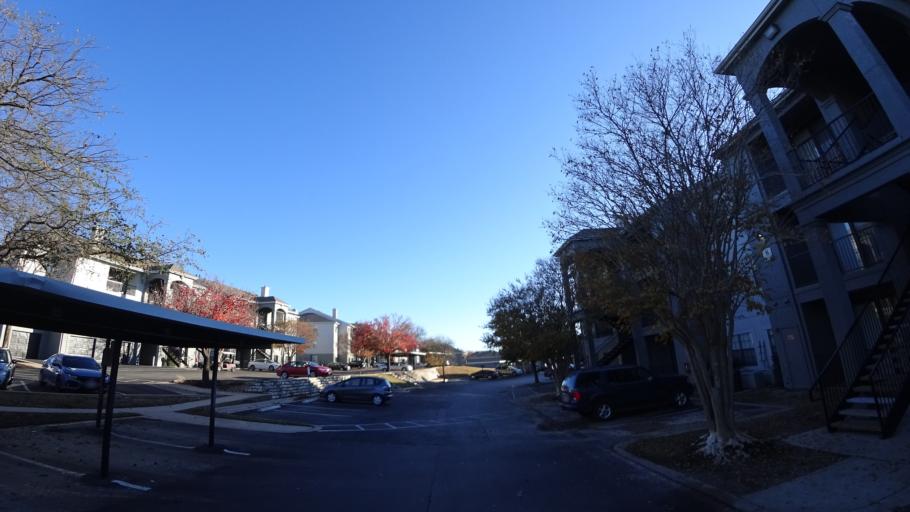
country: US
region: Texas
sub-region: Travis County
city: Wells Branch
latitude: 30.4042
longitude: -97.7067
